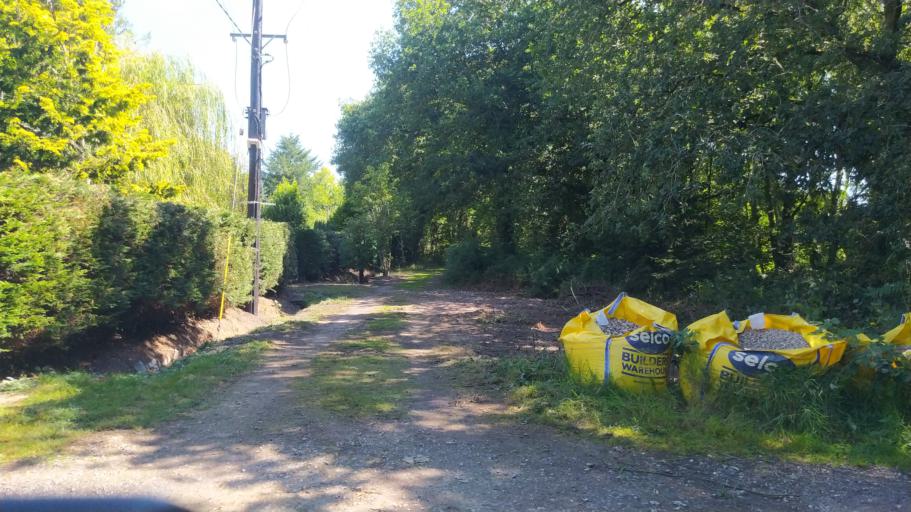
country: GB
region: England
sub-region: Dorset
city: Wareham
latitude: 50.6808
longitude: -2.1544
